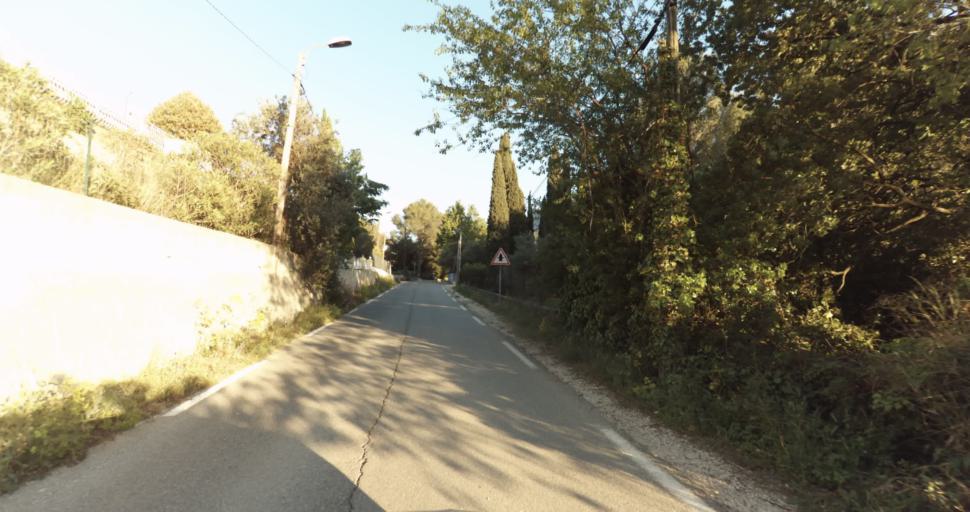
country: FR
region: Provence-Alpes-Cote d'Azur
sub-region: Departement du Var
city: Le Revest-les-Eaux
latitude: 43.1678
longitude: 5.9361
